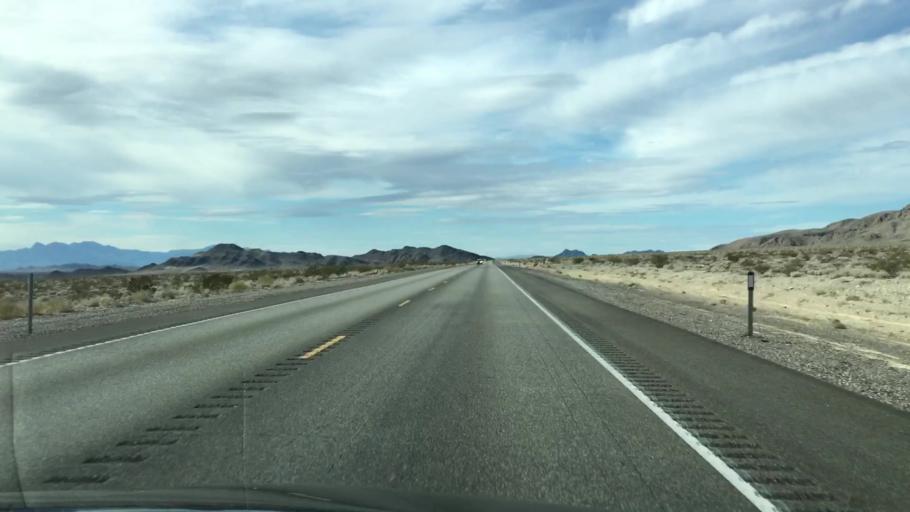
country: US
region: Nevada
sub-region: Nye County
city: Pahrump
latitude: 36.5715
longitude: -116.1703
